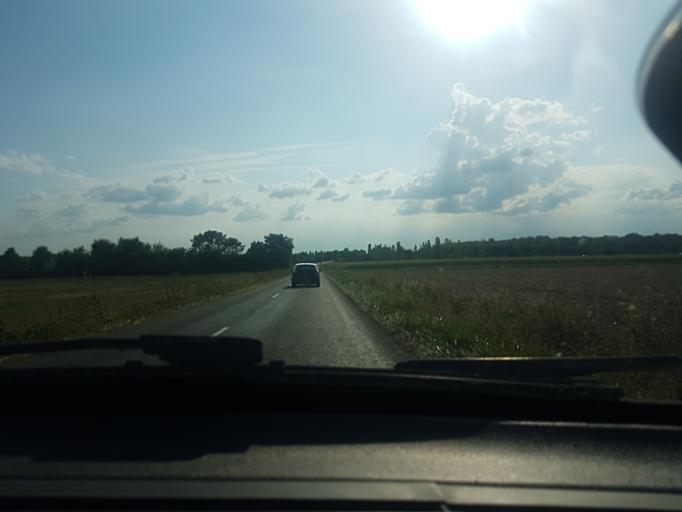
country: FR
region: Bourgogne
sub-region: Departement de Saone-et-Loire
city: Varennes-le-Grand
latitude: 46.7019
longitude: 4.8504
